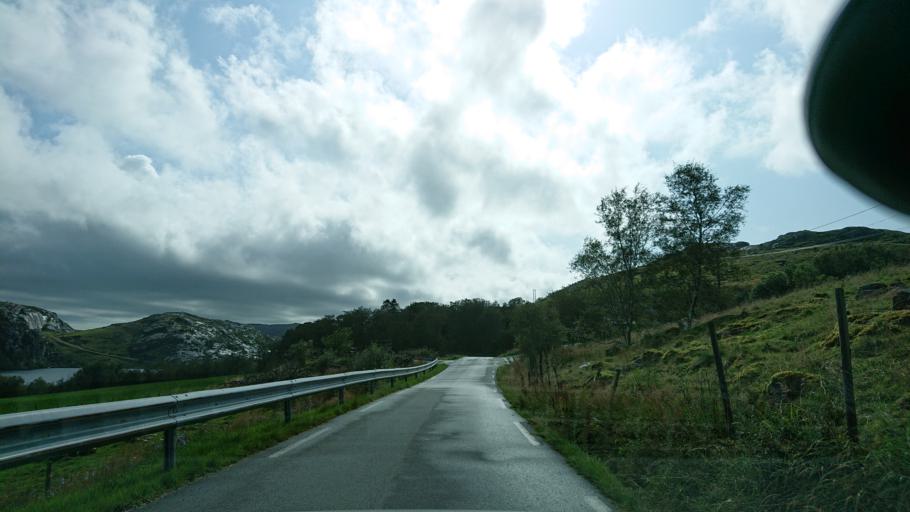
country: NO
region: Rogaland
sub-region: Gjesdal
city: Algard
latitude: 58.6938
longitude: 5.8825
